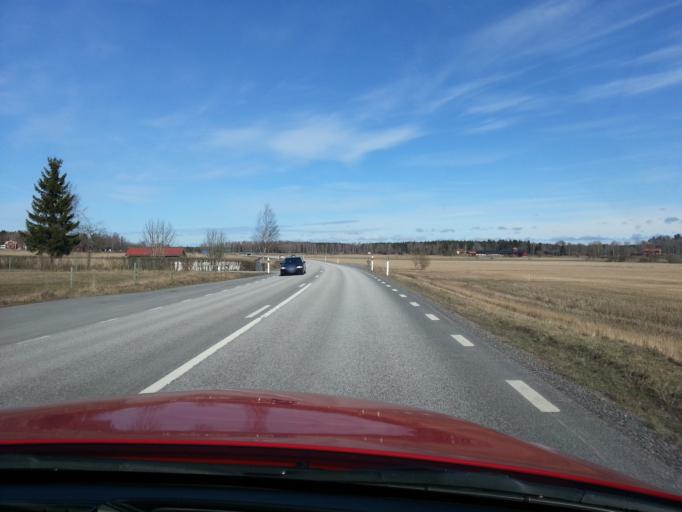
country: SE
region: Uppsala
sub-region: Osthammars Kommun
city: Gimo
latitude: 60.1565
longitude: 18.1895
